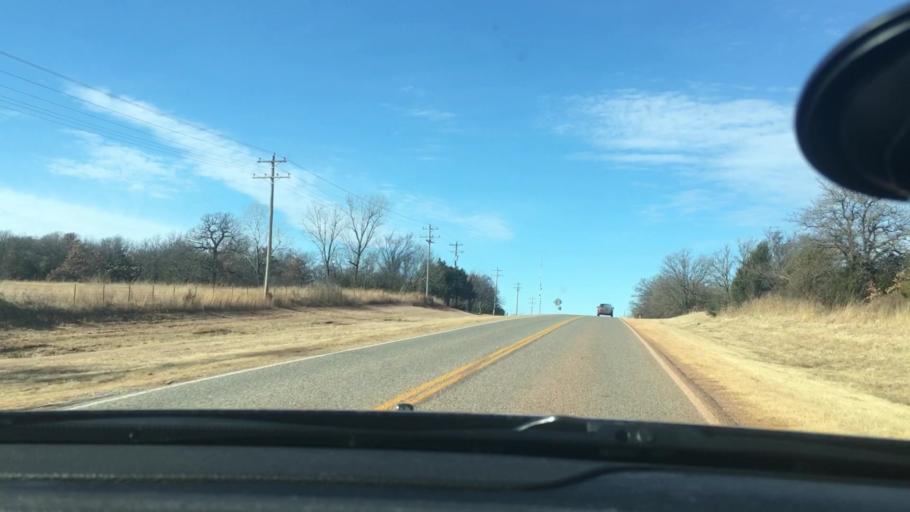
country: US
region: Oklahoma
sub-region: Cleveland County
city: Lexington
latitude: 35.0150
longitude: -97.1714
